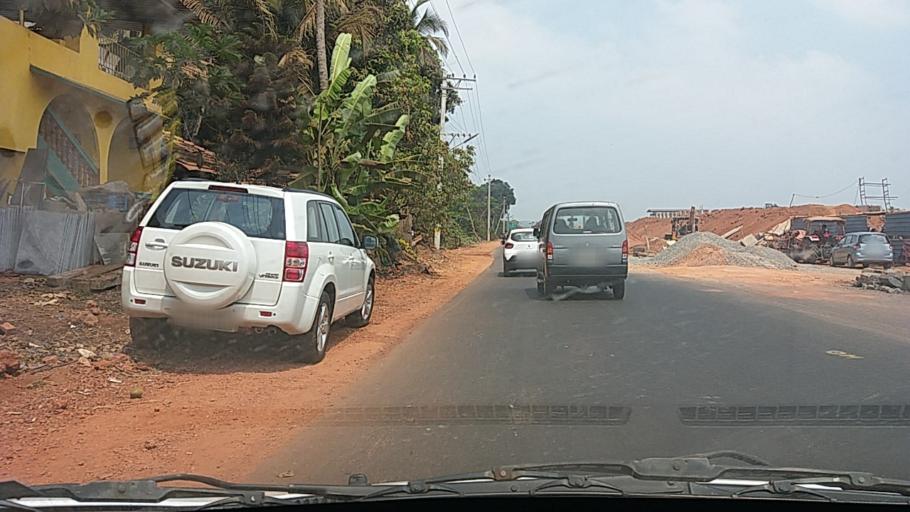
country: IN
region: Goa
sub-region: North Goa
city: Bambolim
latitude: 15.4761
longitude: 73.8492
